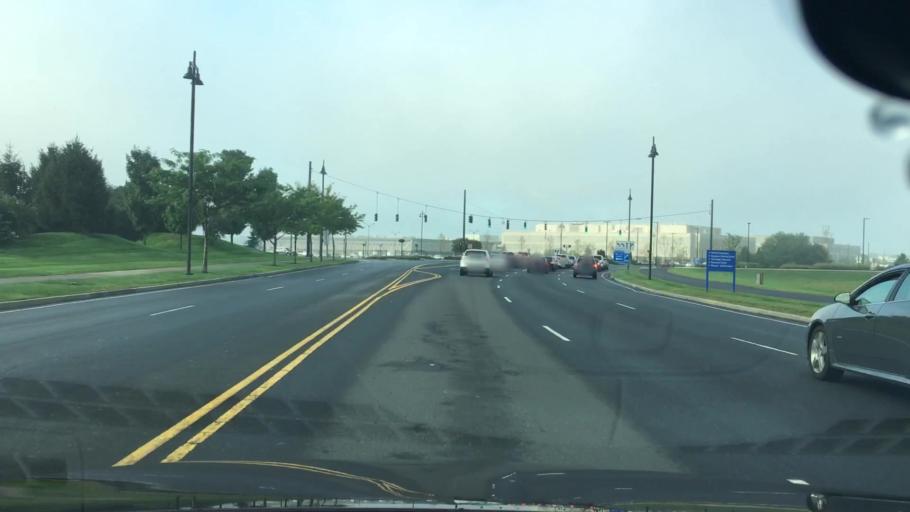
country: US
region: Connecticut
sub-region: Hartford County
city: East Hartford
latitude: 41.7565
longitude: -72.6235
